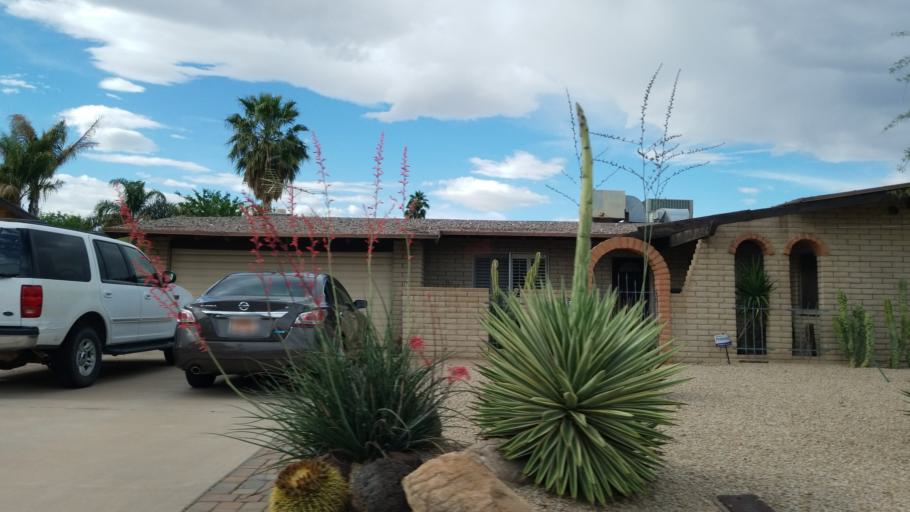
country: US
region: Arizona
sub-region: Maricopa County
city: Paradise Valley
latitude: 33.5891
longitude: -111.9996
